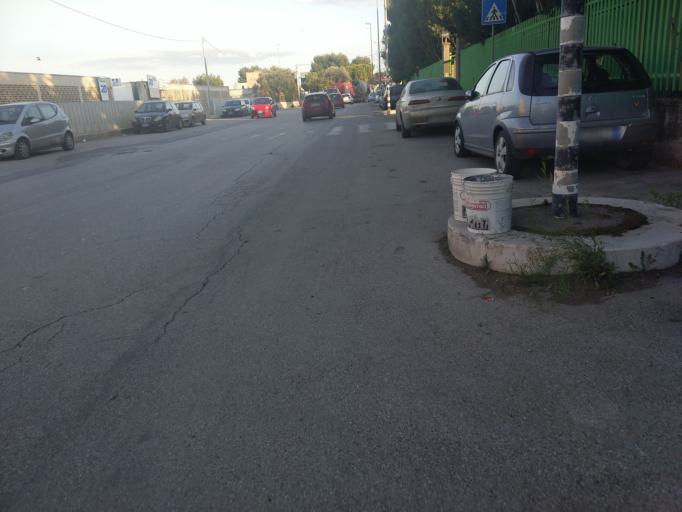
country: IT
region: Apulia
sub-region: Provincia di Bari
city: Bari
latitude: 41.1147
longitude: 16.8401
